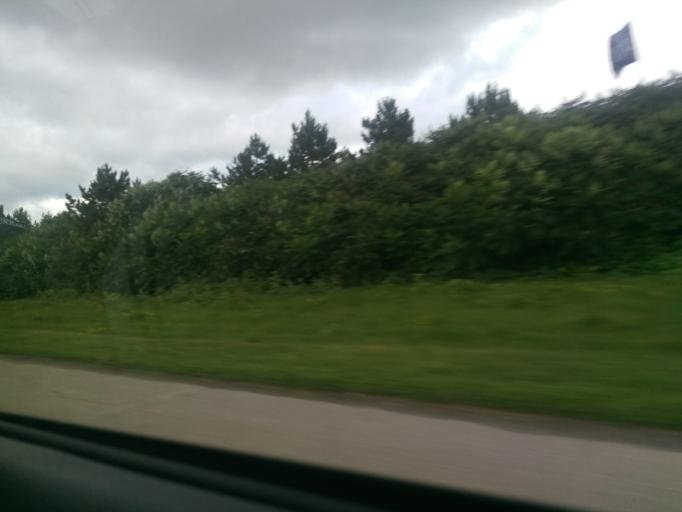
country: CA
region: Quebec
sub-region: Outaouais
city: Gatineau
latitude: 45.4755
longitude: -75.7427
